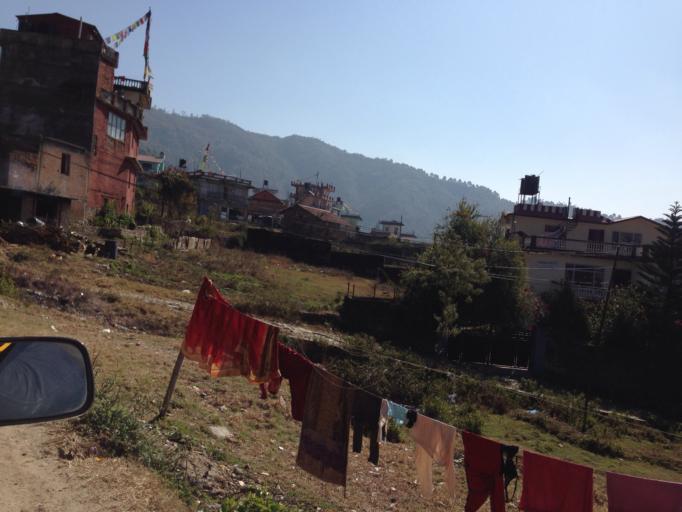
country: NP
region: Central Region
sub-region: Bagmati Zone
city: Kathmandu
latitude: 27.7786
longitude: 85.3668
